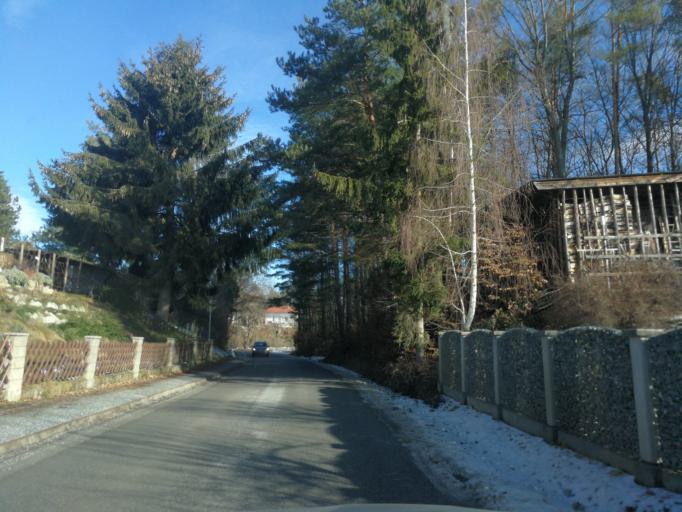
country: AT
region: Styria
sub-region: Politischer Bezirk Graz-Umgebung
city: Eggersdorf bei Graz
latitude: 47.0863
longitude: 15.5879
